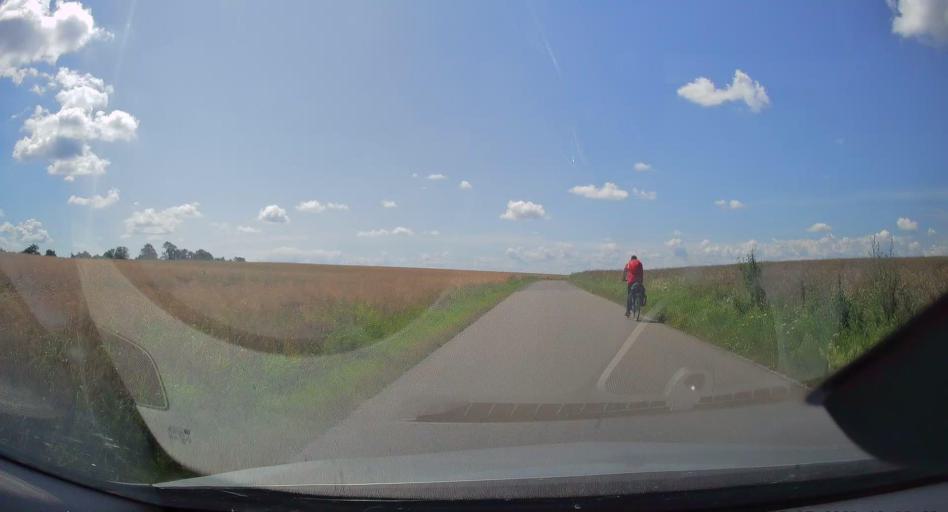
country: PL
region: Subcarpathian Voivodeship
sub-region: Powiat jaroslawski
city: Sosnica
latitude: 49.8586
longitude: 22.8805
